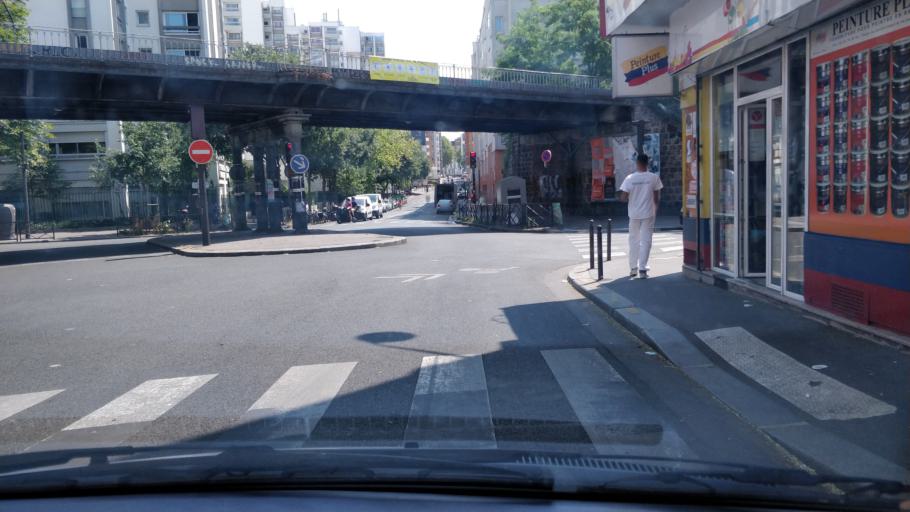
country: FR
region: Ile-de-France
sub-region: Departement de Seine-Saint-Denis
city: Bagnolet
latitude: 48.8562
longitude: 2.4052
